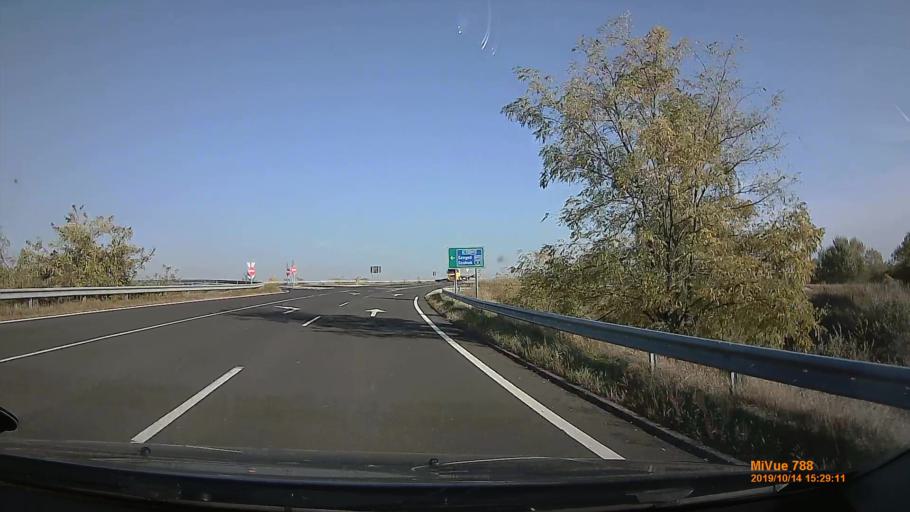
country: HU
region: Pest
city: Ecser
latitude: 47.4314
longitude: 19.3238
